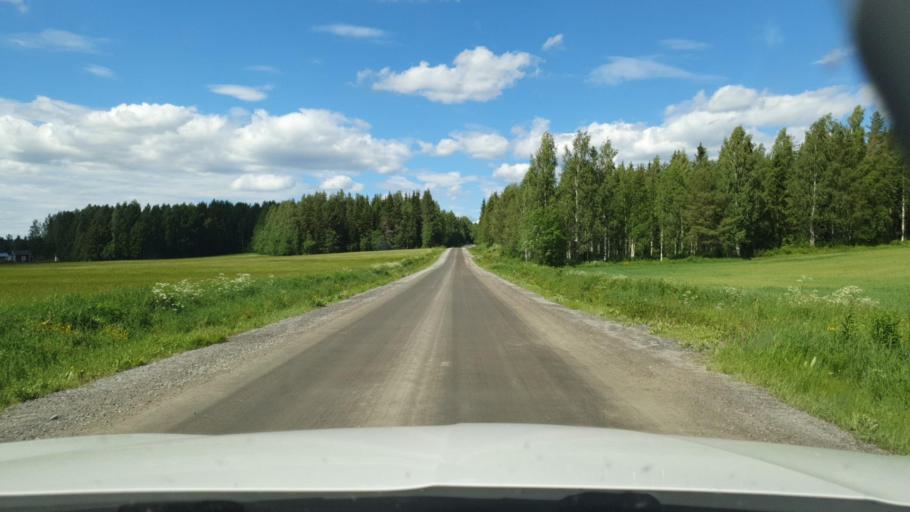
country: SE
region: Vaesterbotten
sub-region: Skelleftea Kommun
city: Forsbacka
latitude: 64.7909
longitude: 20.5091
